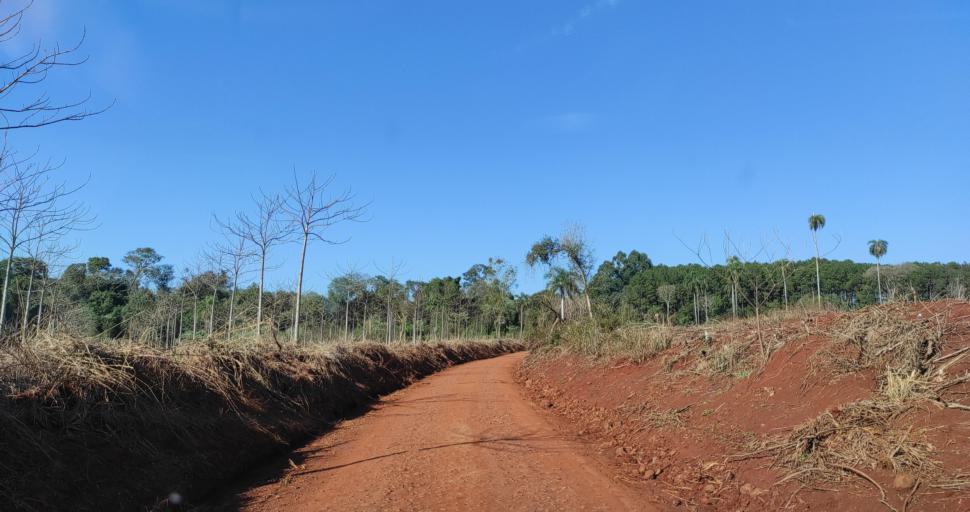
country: AR
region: Misiones
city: Capiovi
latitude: -26.8688
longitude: -55.0425
